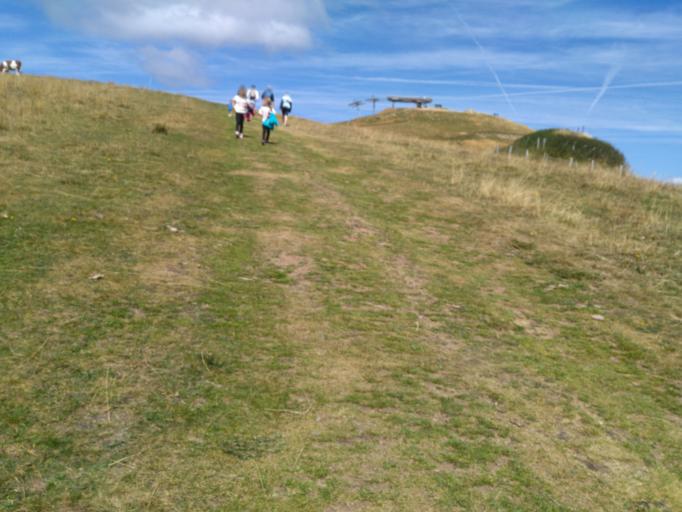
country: FR
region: Rhone-Alpes
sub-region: Departement de la Haute-Savoie
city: Viuz-la-Chiesaz
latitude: 45.7945
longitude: 6.1020
